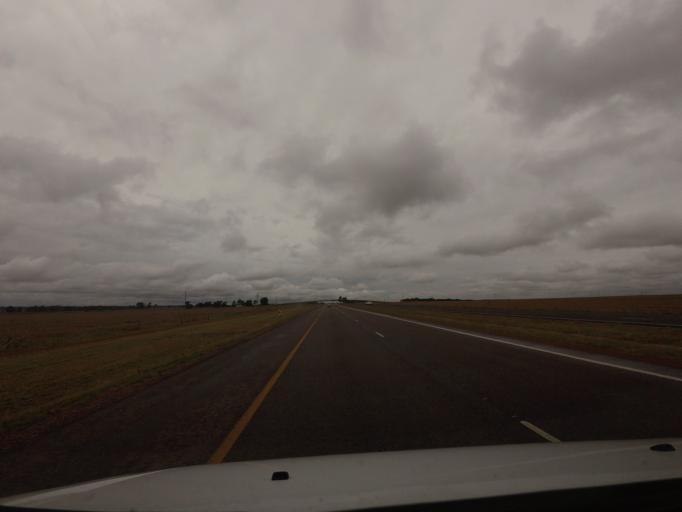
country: ZA
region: Mpumalanga
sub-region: Nkangala District Municipality
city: Middelburg
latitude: -25.8214
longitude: 29.6295
